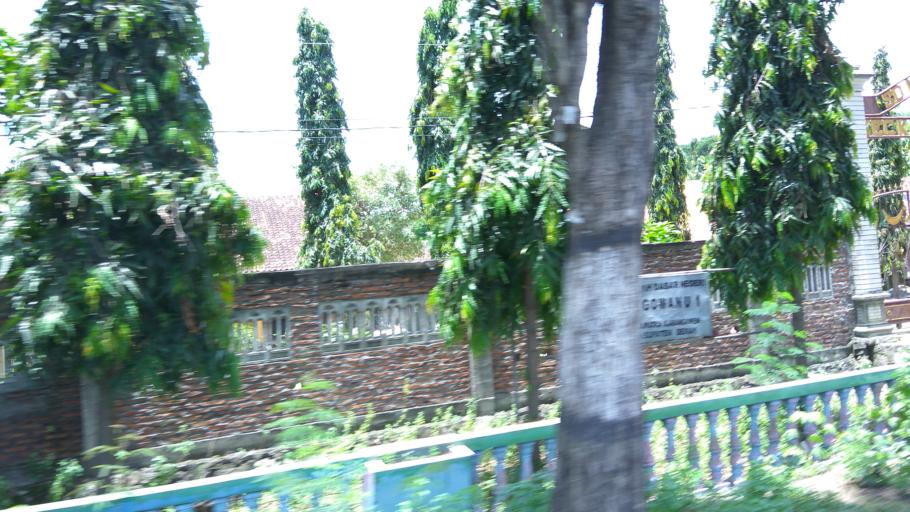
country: ID
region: Central Java
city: Mranggen
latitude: -7.0485
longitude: 110.5941
